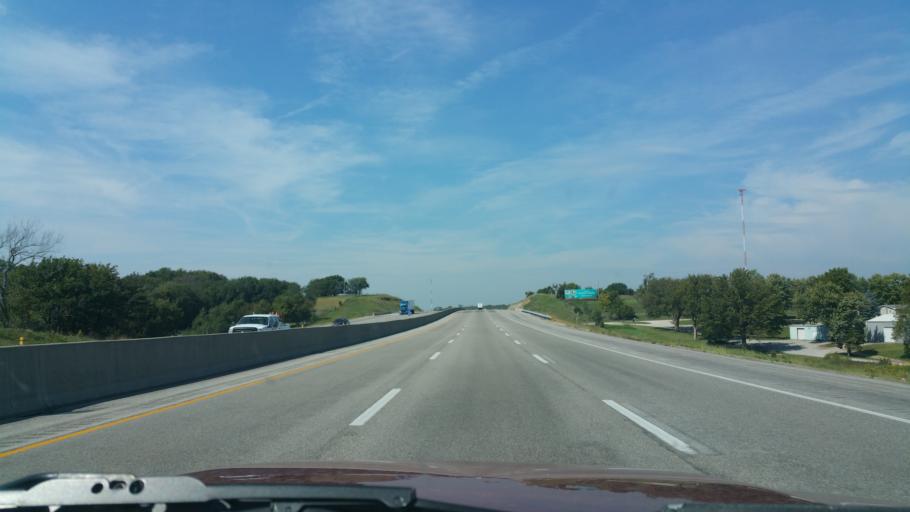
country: US
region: Kansas
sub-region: Shawnee County
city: Topeka
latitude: 39.0151
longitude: -95.4798
